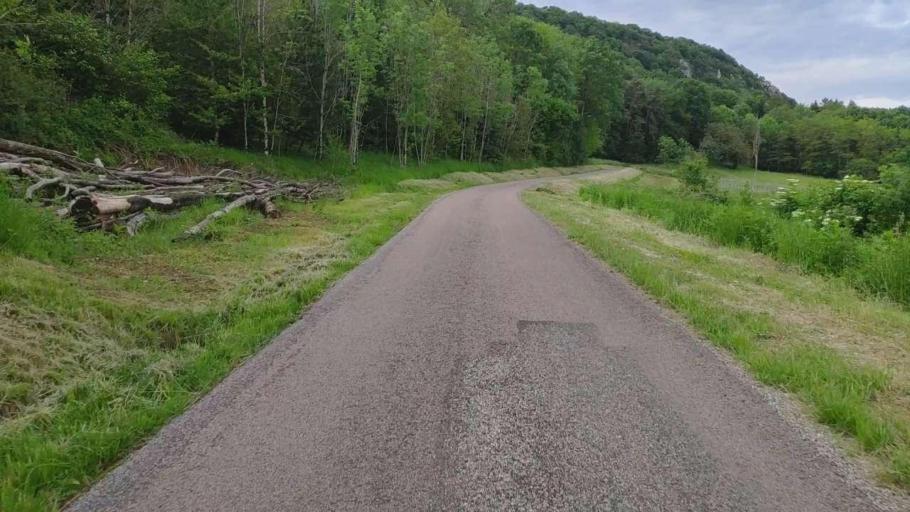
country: FR
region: Franche-Comte
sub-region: Departement du Jura
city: Perrigny
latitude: 46.7175
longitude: 5.6022
